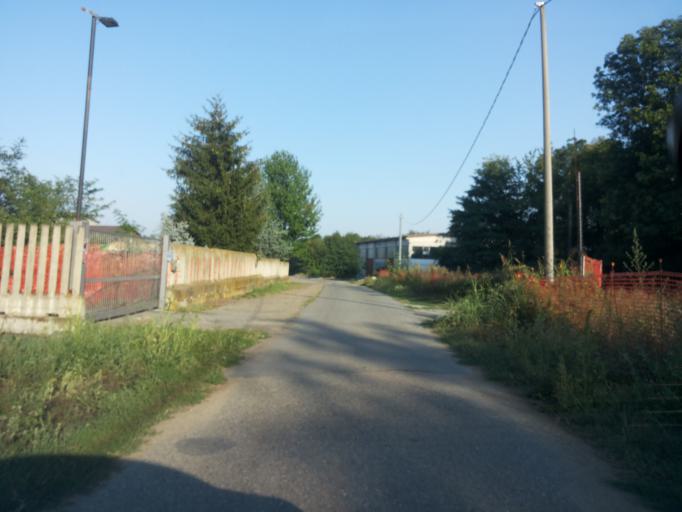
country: IT
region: Piedmont
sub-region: Provincia di Biella
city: Cavaglia
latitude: 45.3927
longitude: 8.1188
